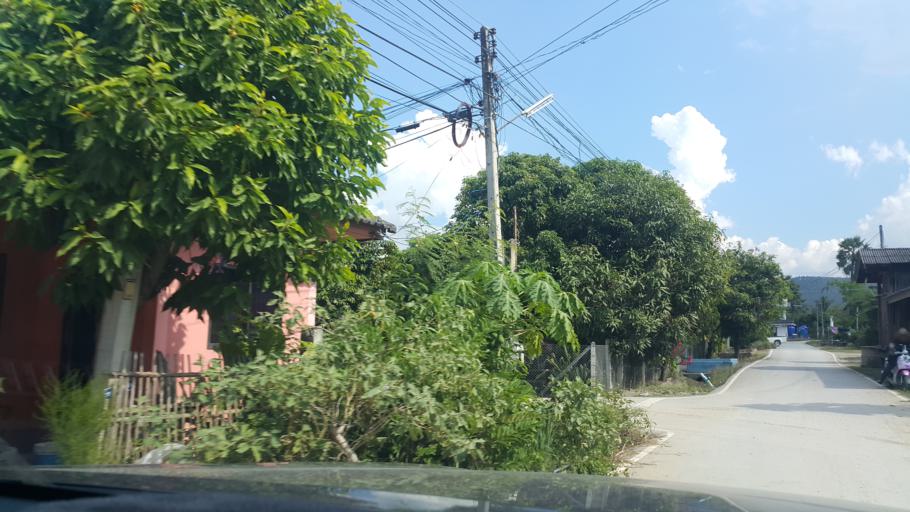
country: TH
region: Chiang Mai
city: San Kamphaeng
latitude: 18.7218
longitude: 99.1698
